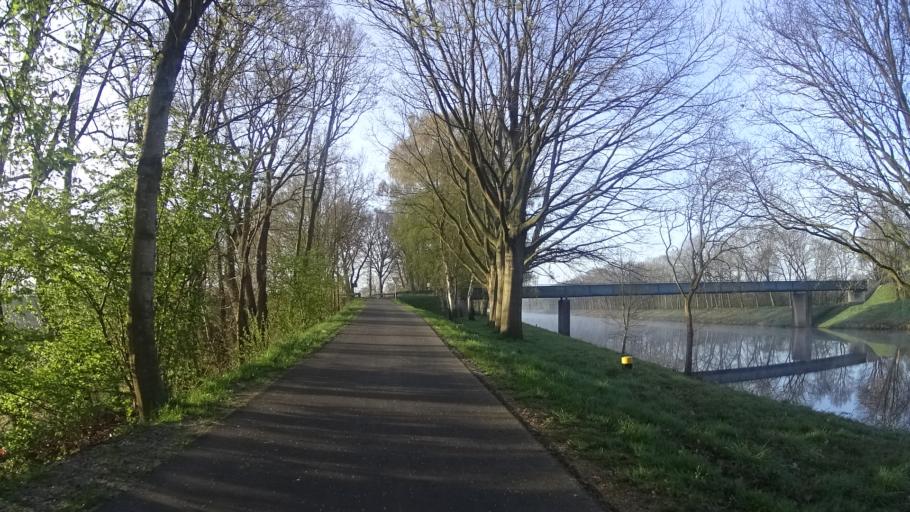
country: DE
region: Lower Saxony
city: Fresenburg
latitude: 52.8961
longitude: 7.3131
